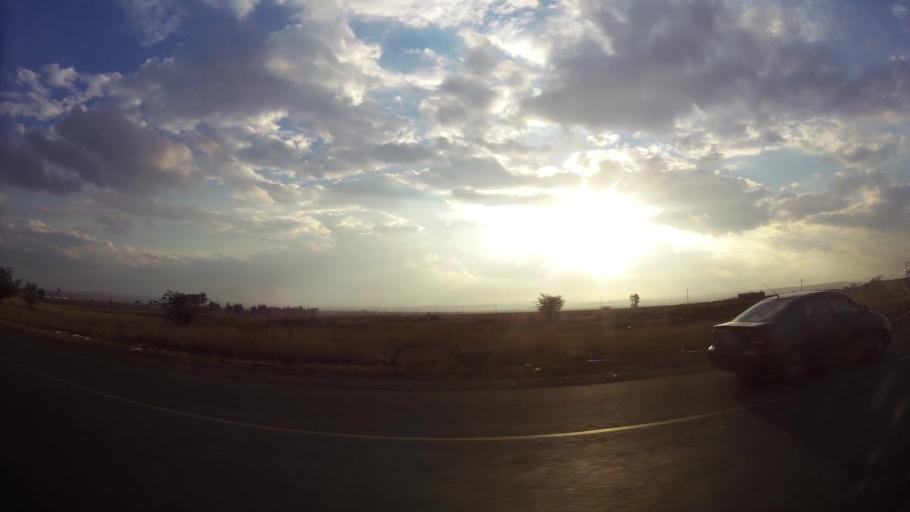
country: ZA
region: Gauteng
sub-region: Sedibeng District Municipality
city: Vanderbijlpark
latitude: -26.5970
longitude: 27.8196
